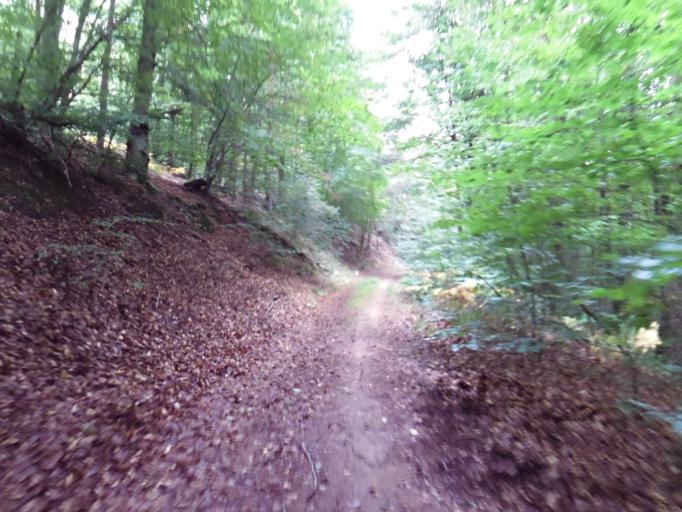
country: DE
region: Rheinland-Pfalz
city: Neuhemsbach
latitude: 49.5053
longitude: 7.9627
